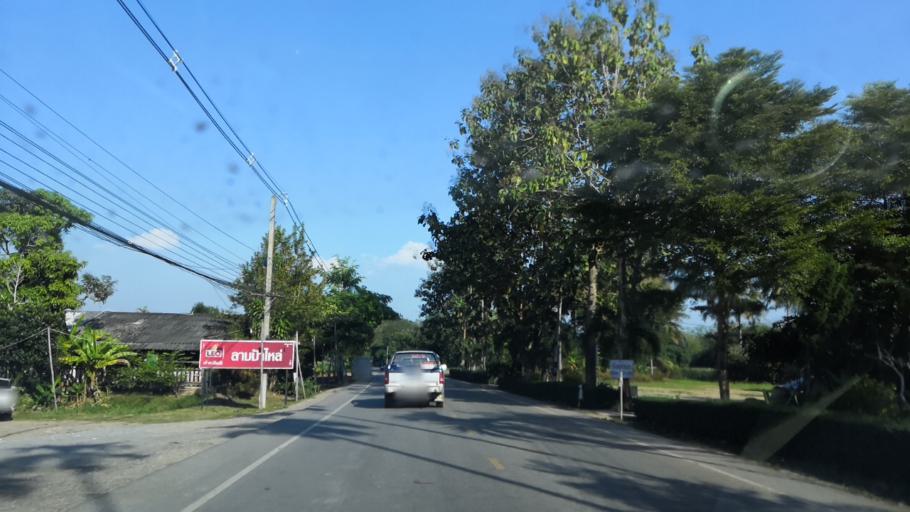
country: TH
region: Chiang Rai
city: Wiang Chai
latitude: 19.9324
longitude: 99.8979
